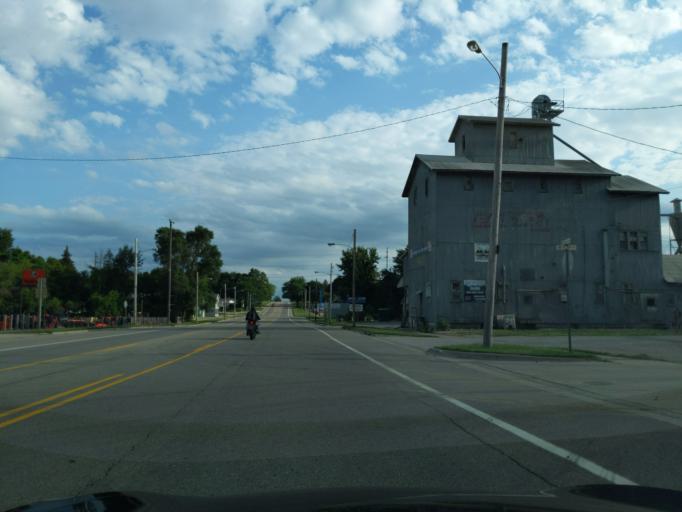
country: US
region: Michigan
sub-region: Clare County
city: Clare
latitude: 43.8176
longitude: -84.7684
